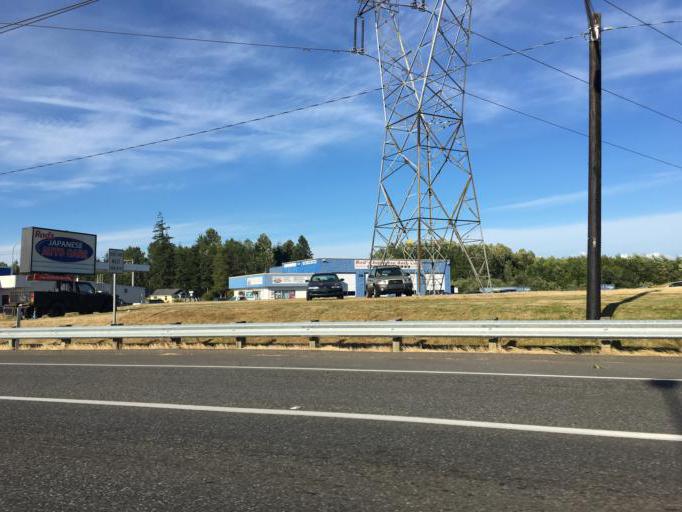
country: US
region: Washington
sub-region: Whatcom County
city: Bellingham
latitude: 48.8323
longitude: -122.4860
